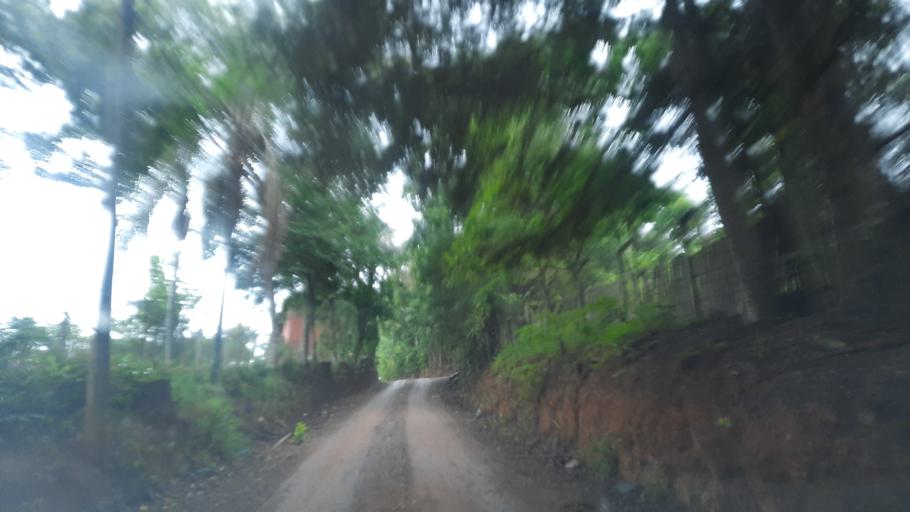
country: BR
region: Sao Paulo
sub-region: Atibaia
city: Atibaia
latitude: -23.0737
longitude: -46.5076
